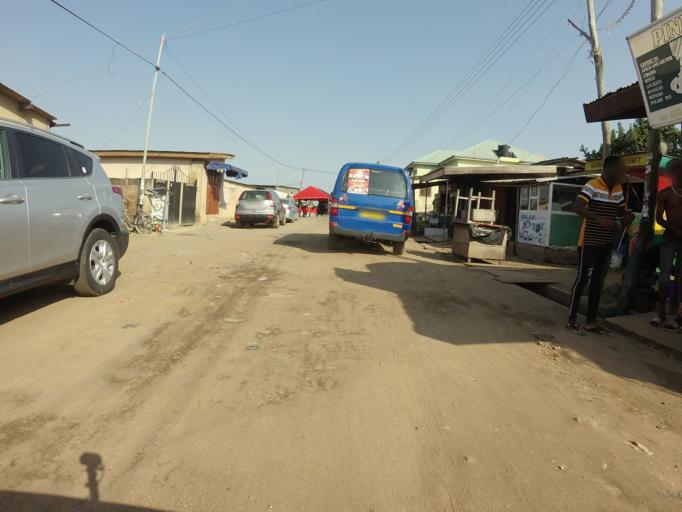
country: GH
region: Greater Accra
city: Dome
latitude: 5.6130
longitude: -0.2338
